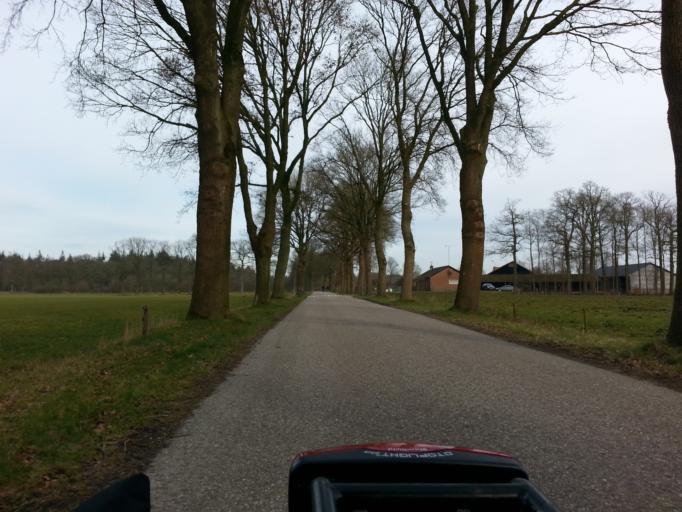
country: NL
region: Utrecht
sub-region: Gemeente Woudenberg
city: Woudenberg
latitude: 52.0903
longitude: 5.3891
